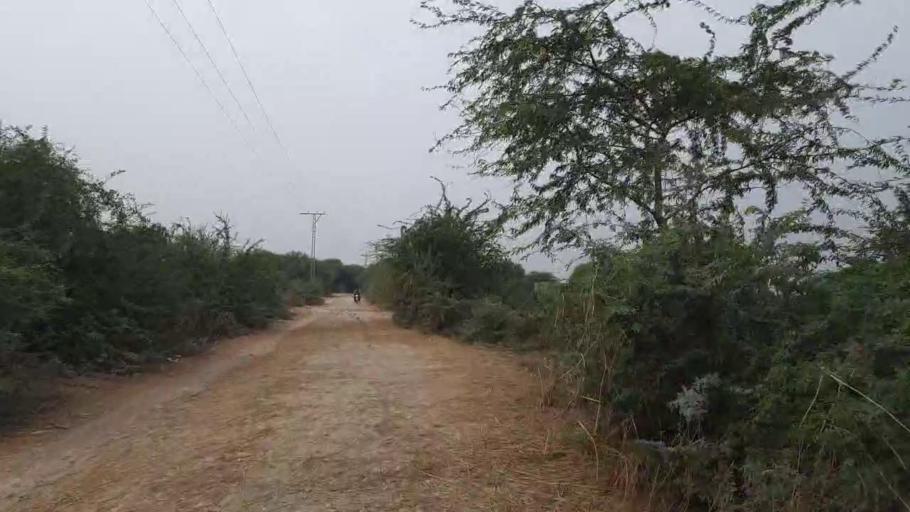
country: PK
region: Sindh
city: Kario
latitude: 24.9243
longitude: 68.5533
